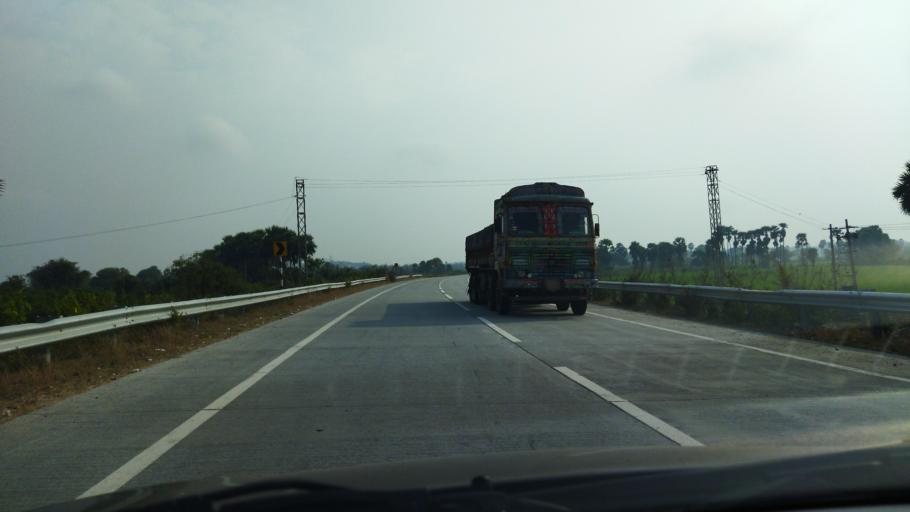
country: IN
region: Telangana
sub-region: Nalgonda
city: Nalgonda
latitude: 17.1764
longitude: 79.3995
